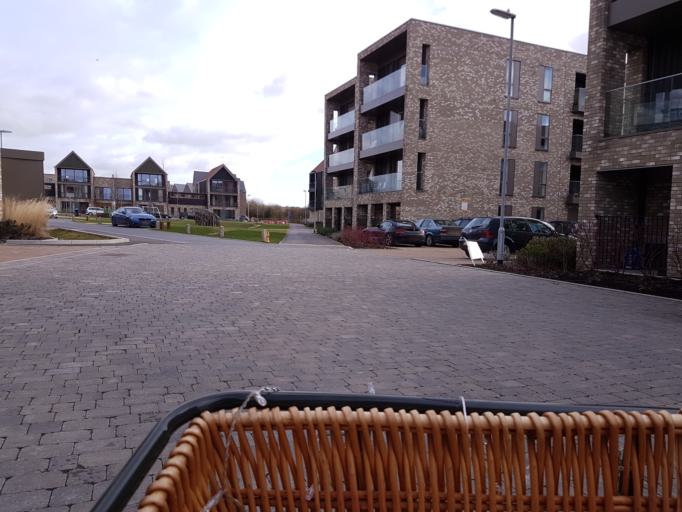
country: GB
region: England
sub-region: Cambridgeshire
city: Cambridge
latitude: 52.1723
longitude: 0.1418
